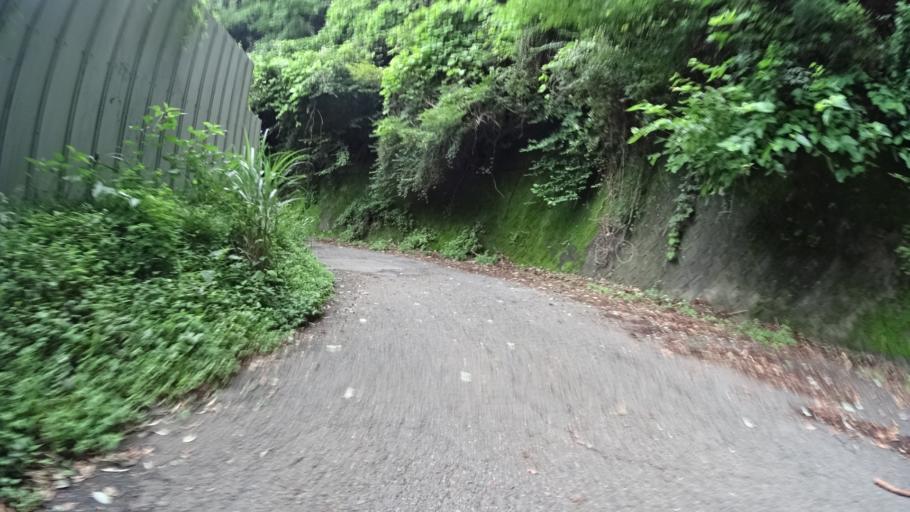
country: JP
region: Kanagawa
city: Atsugi
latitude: 35.5006
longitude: 139.2659
